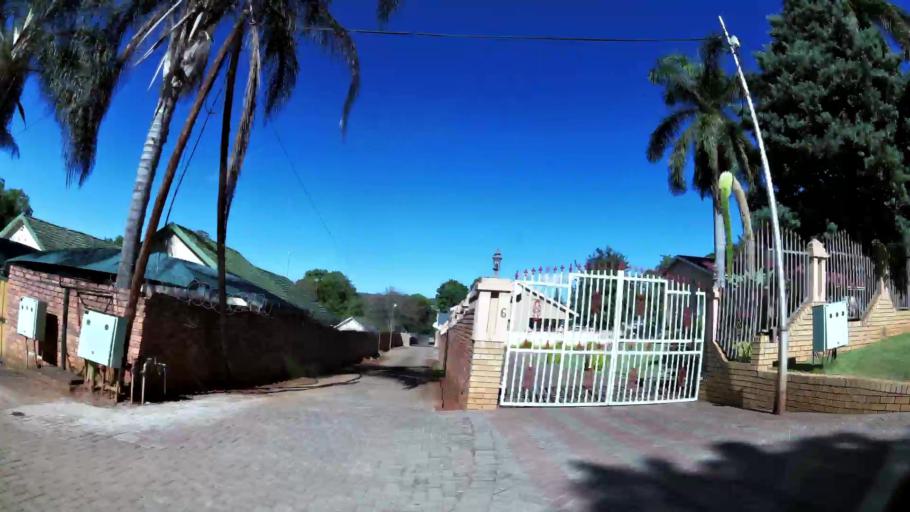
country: ZA
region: Limpopo
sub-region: Mopani District Municipality
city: Tzaneen
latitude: -23.8370
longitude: 30.1559
